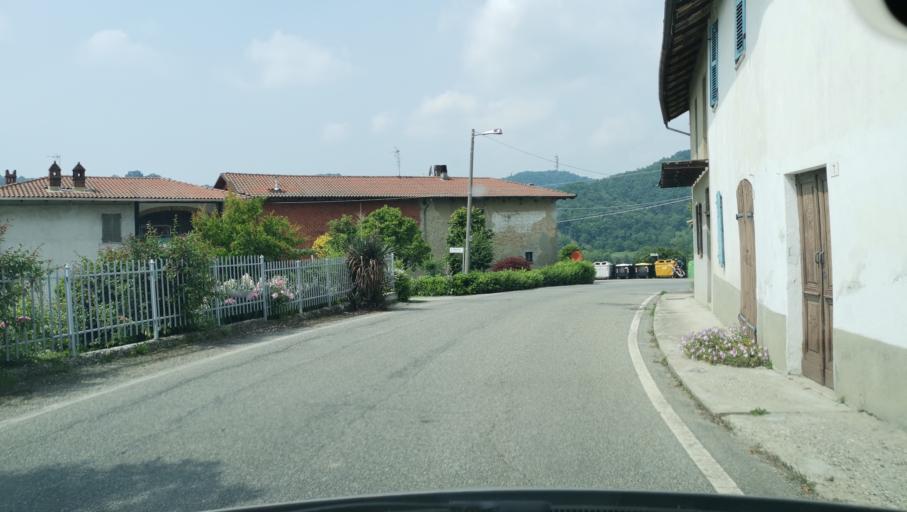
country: IT
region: Piedmont
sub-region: Provincia di Alessandria
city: Odalengo Piccolo
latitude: 45.0710
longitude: 8.2059
